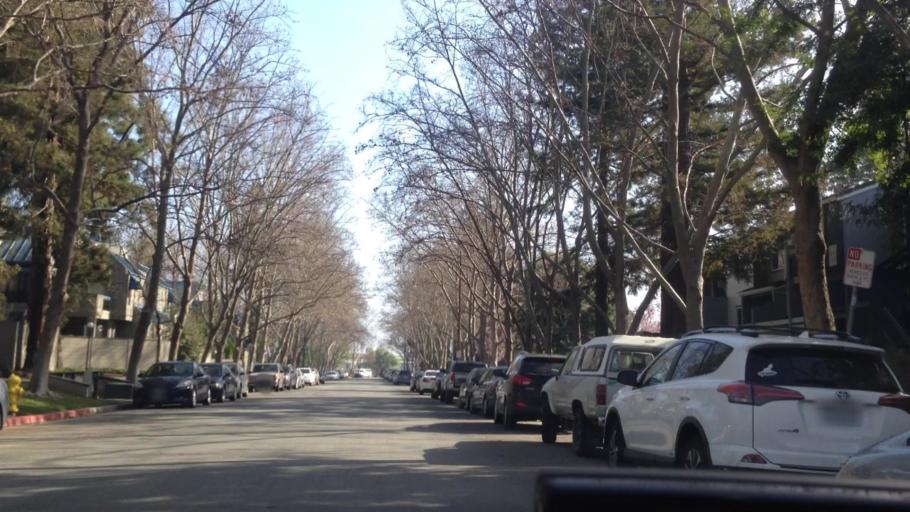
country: US
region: California
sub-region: Santa Clara County
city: Seven Trees
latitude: 37.2527
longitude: -121.8741
